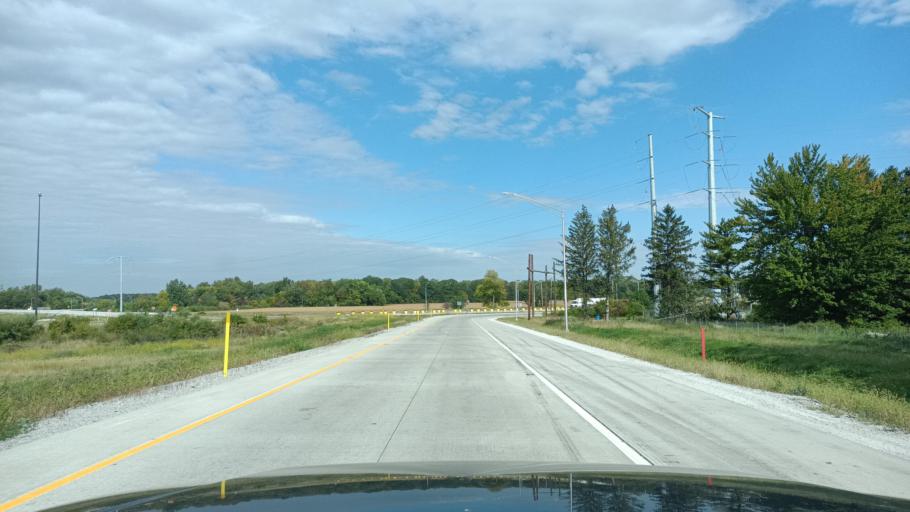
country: US
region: Indiana
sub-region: Allen County
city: New Haven
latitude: 41.0841
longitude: -84.9898
